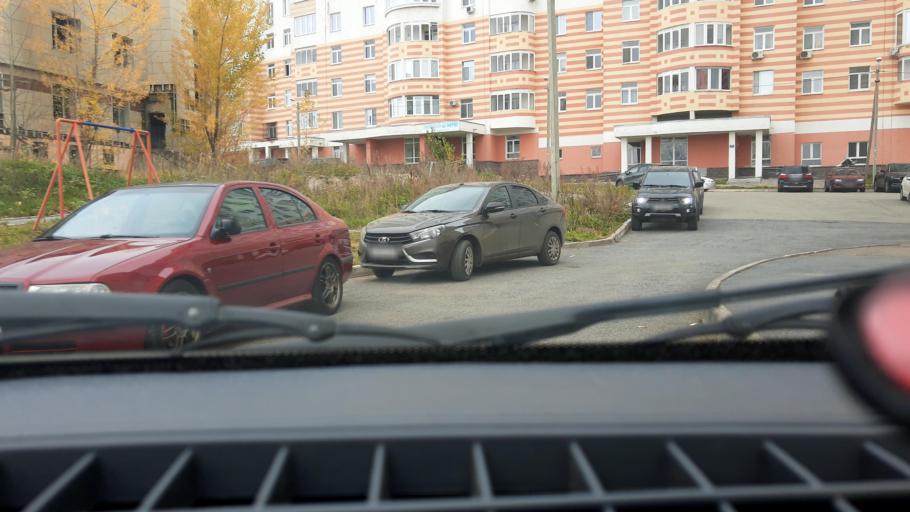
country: RU
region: Bashkortostan
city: Ufa
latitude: 54.7820
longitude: 56.0127
